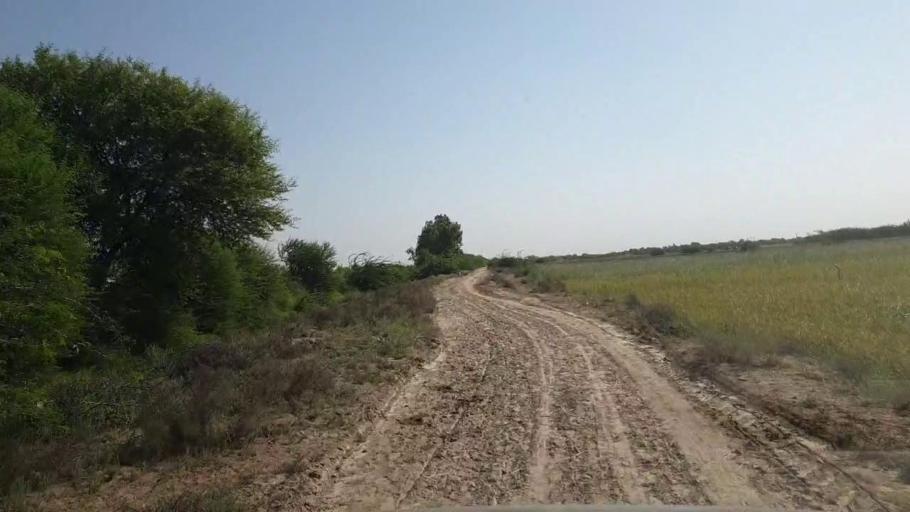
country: PK
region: Sindh
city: Kadhan
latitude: 24.5919
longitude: 69.0075
